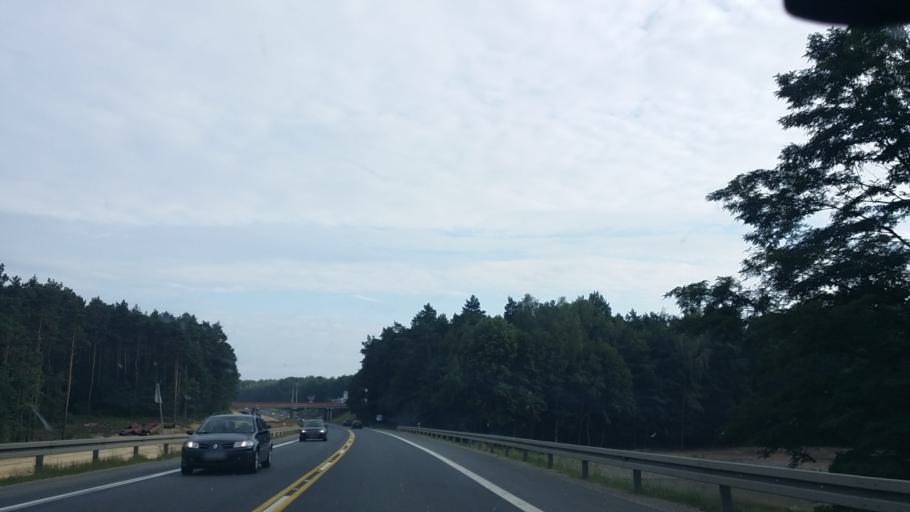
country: PL
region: Lubusz
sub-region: Zielona Gora
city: Zielona Gora
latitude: 51.9419
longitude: 15.5478
